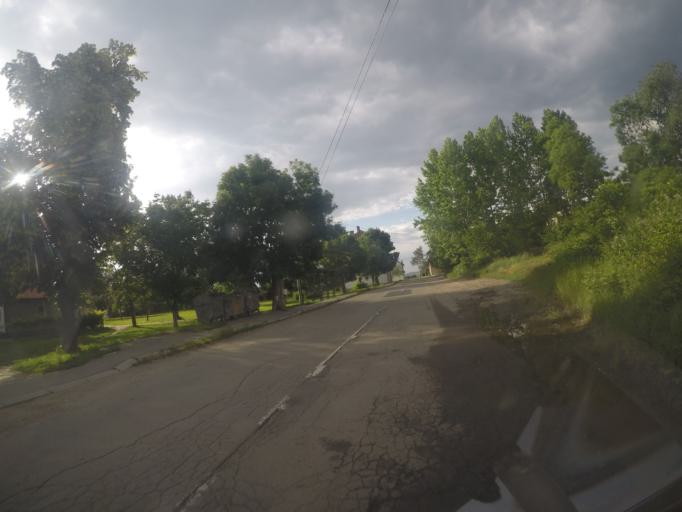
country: RS
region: Central Serbia
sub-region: Belgrade
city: Zemun
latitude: 44.9098
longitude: 20.4300
